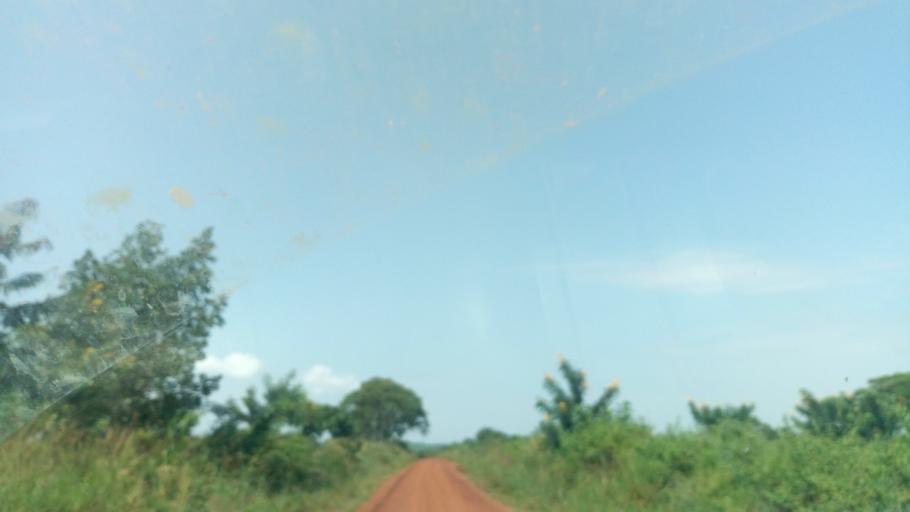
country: UG
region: Western Region
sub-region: Masindi District
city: Masindi
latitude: 1.6812
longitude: 31.8311
